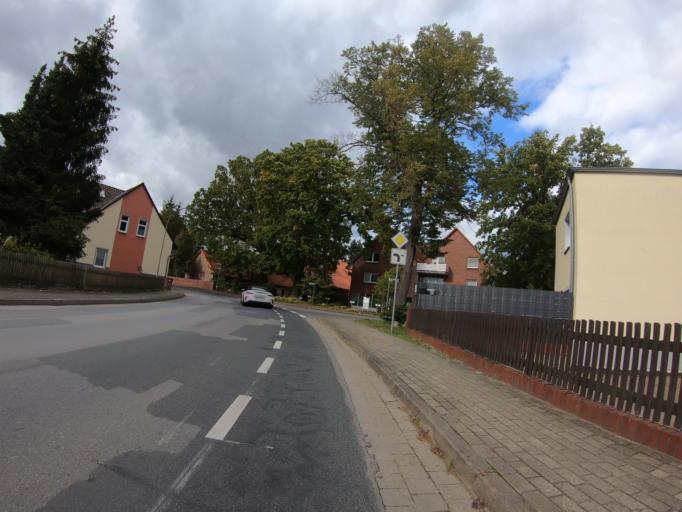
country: DE
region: Lower Saxony
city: Isenbuttel
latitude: 52.4330
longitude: 10.5819
